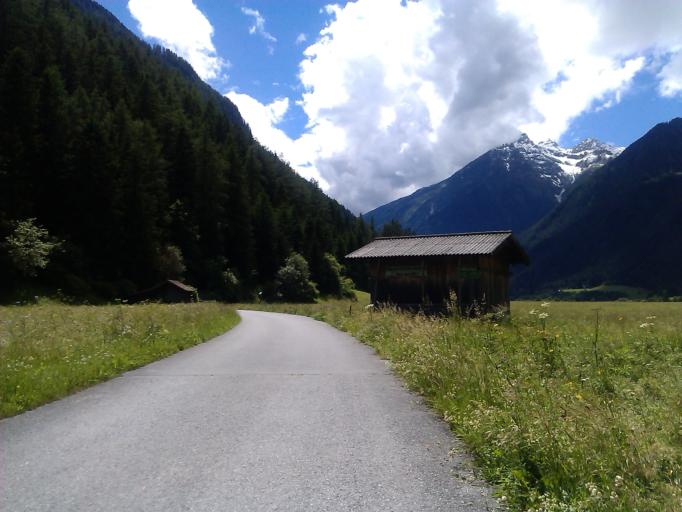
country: AT
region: Tyrol
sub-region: Politischer Bezirk Landeck
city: Pfunds
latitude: 46.9637
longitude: 10.5358
